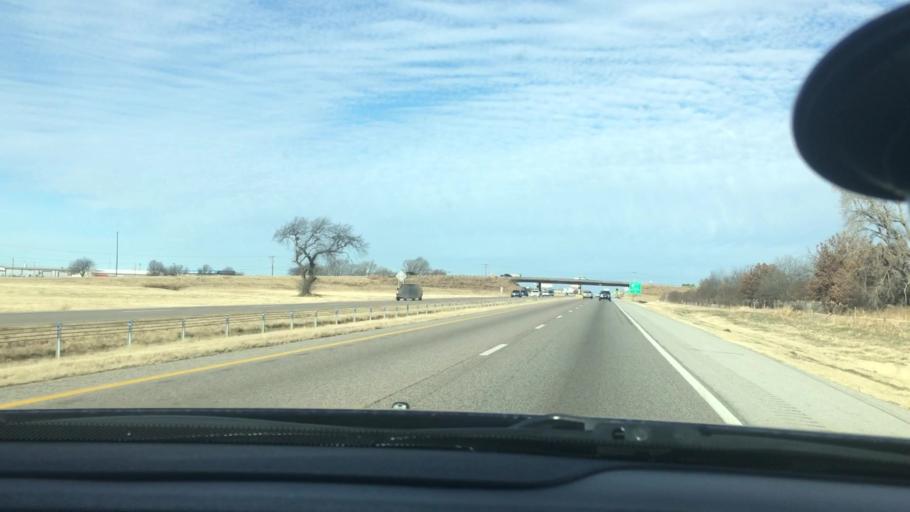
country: US
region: Oklahoma
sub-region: McClain County
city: Goldsby
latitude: 35.1505
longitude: -97.4742
